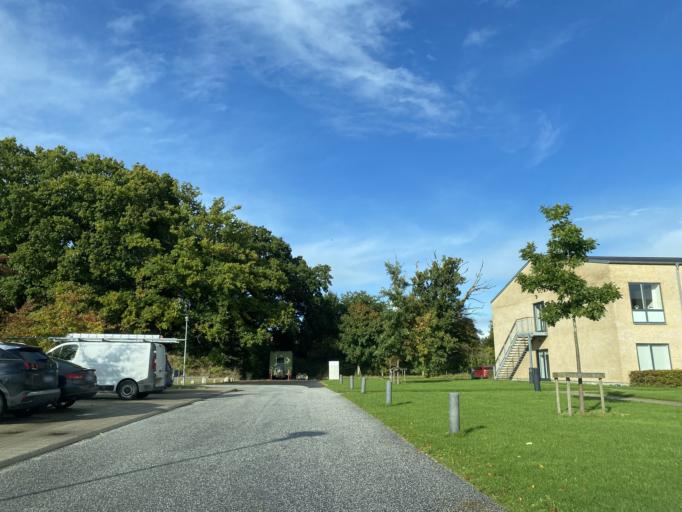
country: DK
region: South Denmark
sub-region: Haderslev Kommune
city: Haderslev
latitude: 55.2462
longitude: 9.4453
